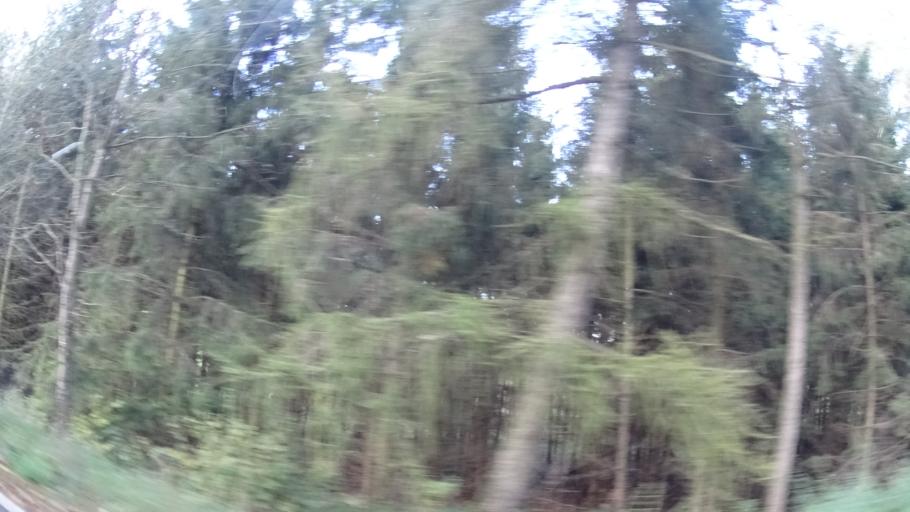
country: DE
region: Baden-Wuerttemberg
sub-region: Karlsruhe Region
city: Hopfingen
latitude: 49.6322
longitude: 9.3957
